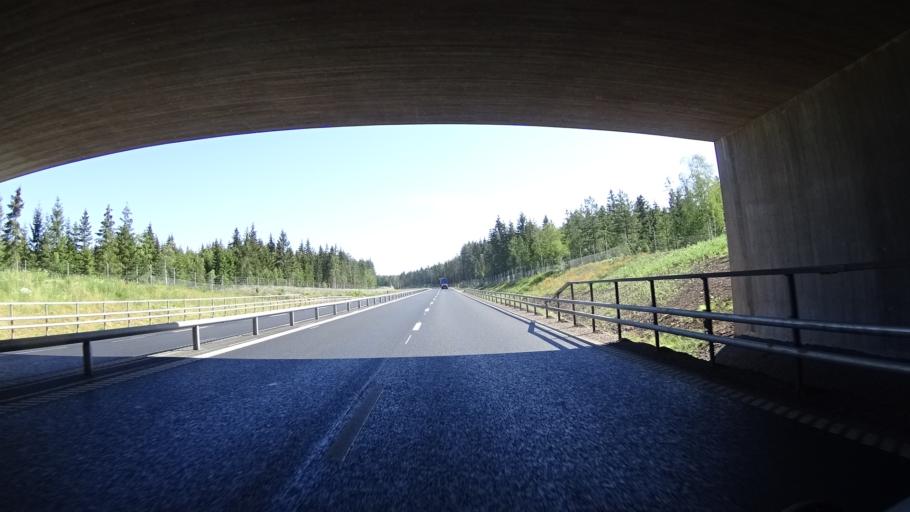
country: SE
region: Vaestra Goetaland
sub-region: Gullspangs Kommun
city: Hova
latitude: 58.8356
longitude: 14.1840
